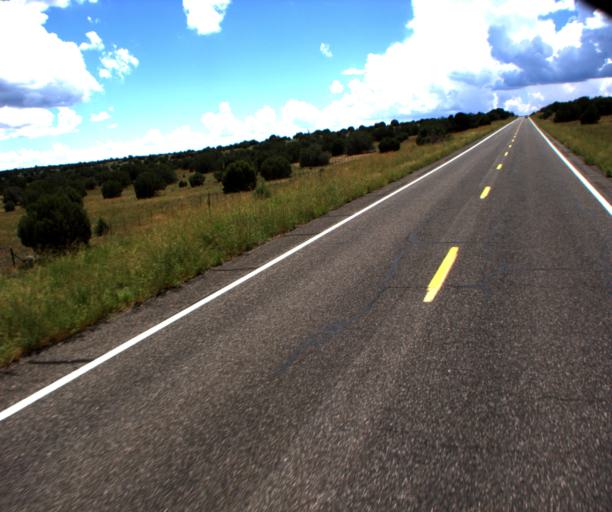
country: US
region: Arizona
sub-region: Gila County
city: Pine
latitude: 34.4968
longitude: -111.5863
